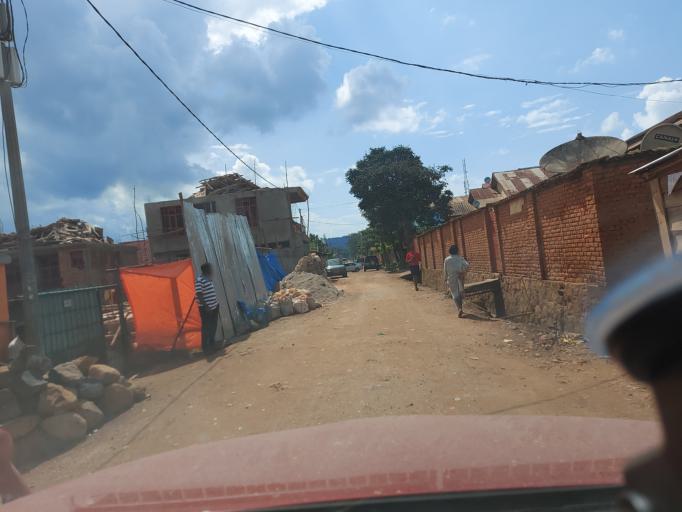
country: RW
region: Western Province
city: Cyangugu
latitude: -2.5000
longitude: 28.8818
